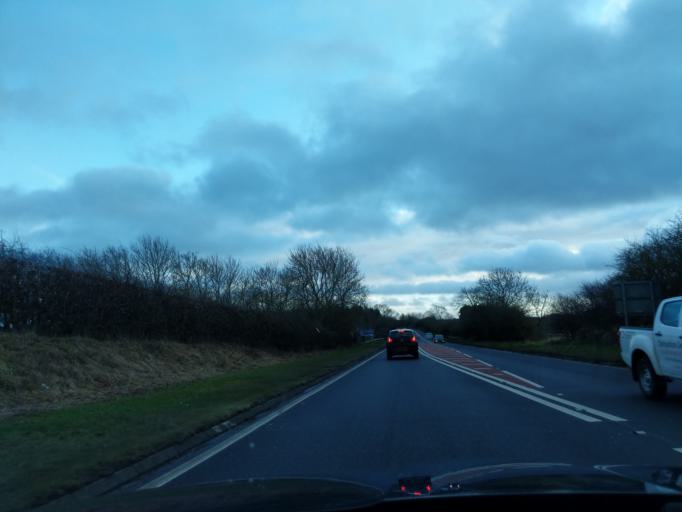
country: GB
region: England
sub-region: Northumberland
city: Felton
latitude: 55.2708
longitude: -1.7219
